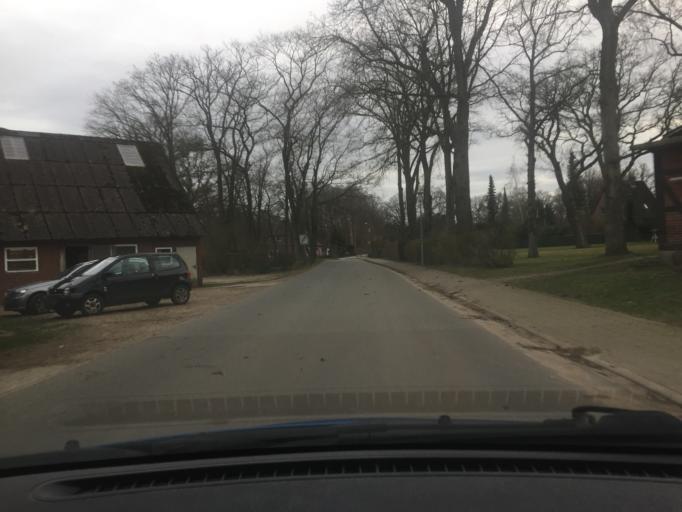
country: DE
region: Lower Saxony
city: Salzhausen
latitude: 53.2204
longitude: 10.1942
